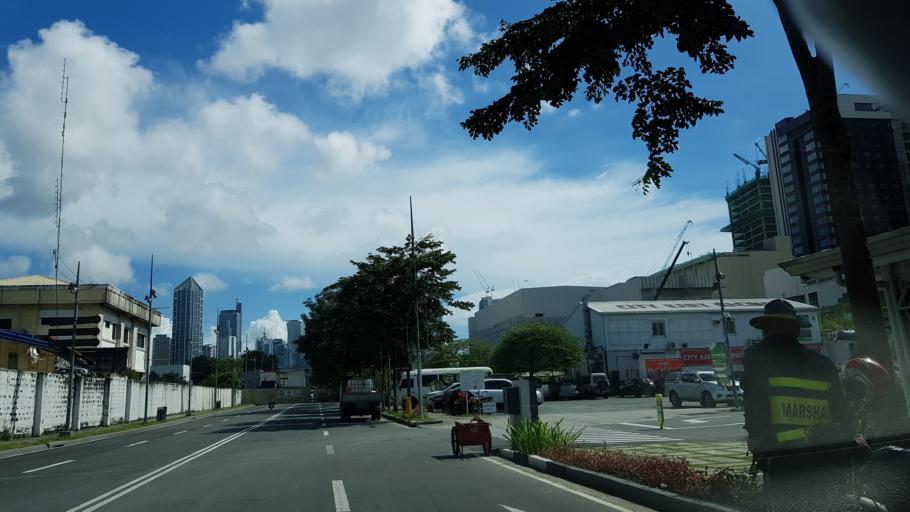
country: PH
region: Metro Manila
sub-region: Mandaluyong
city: Mandaluyong City
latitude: 14.5751
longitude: 121.0210
